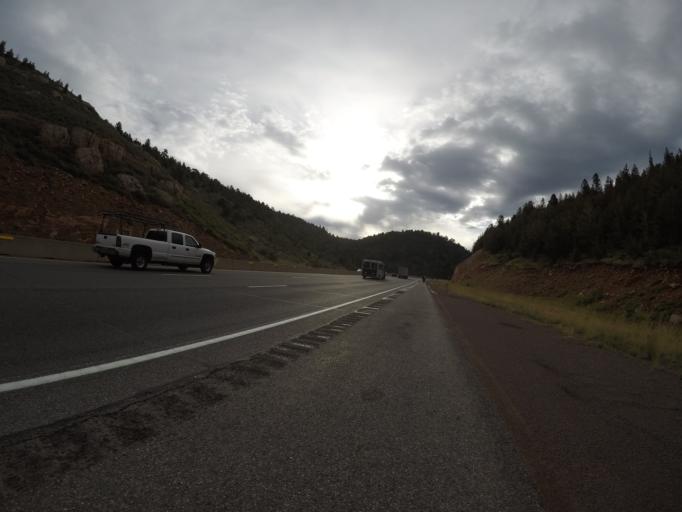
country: US
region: Wyoming
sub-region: Albany County
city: Laramie
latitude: 41.2655
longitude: -105.4717
